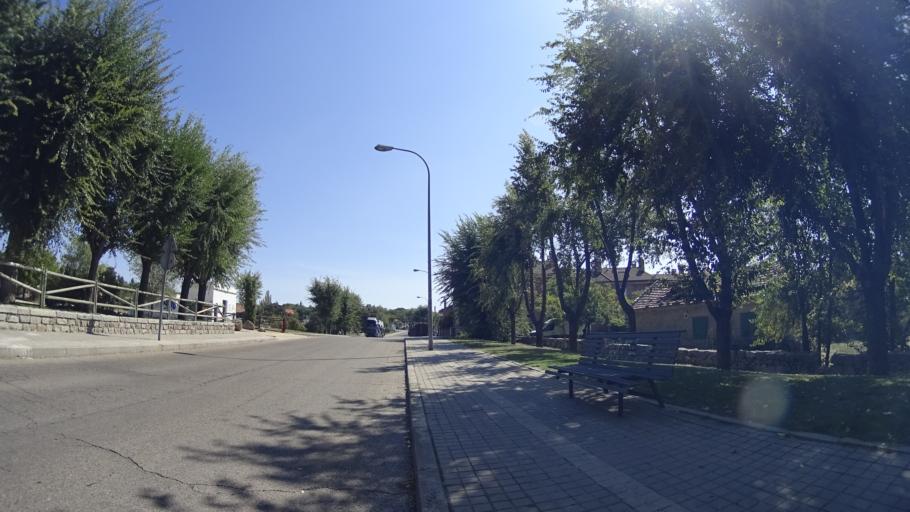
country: ES
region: Madrid
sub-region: Provincia de Madrid
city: Colmenarejo
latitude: 40.5641
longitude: -4.0168
